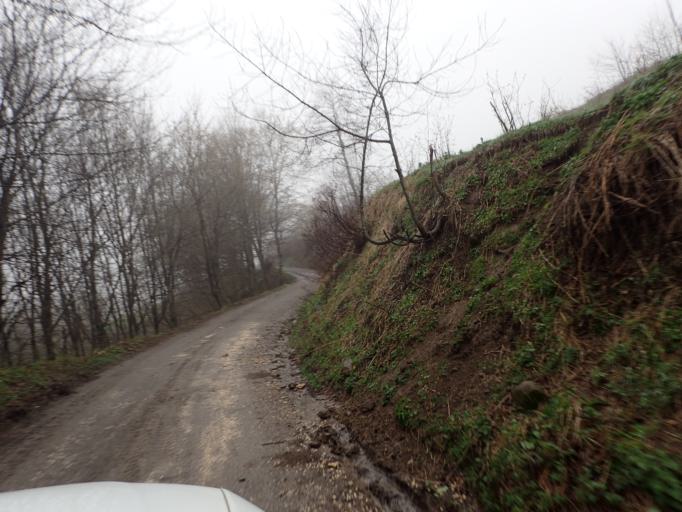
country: TR
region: Ordu
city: Kumru
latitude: 40.8012
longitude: 37.2742
